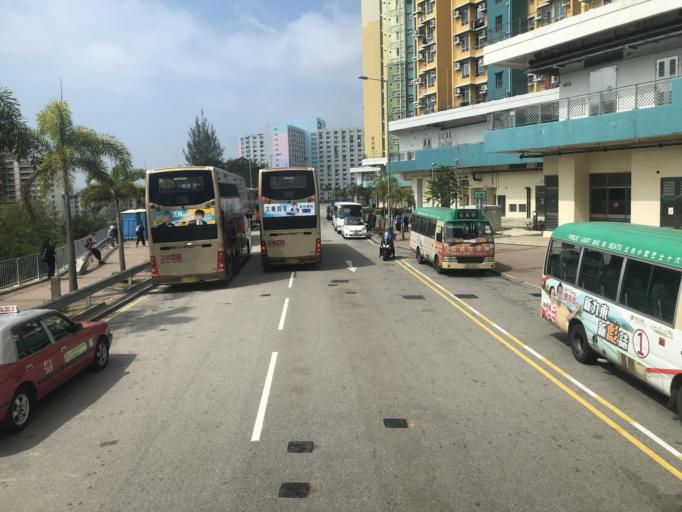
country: HK
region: Kowloon City
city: Kowloon
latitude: 22.3265
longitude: 114.2293
